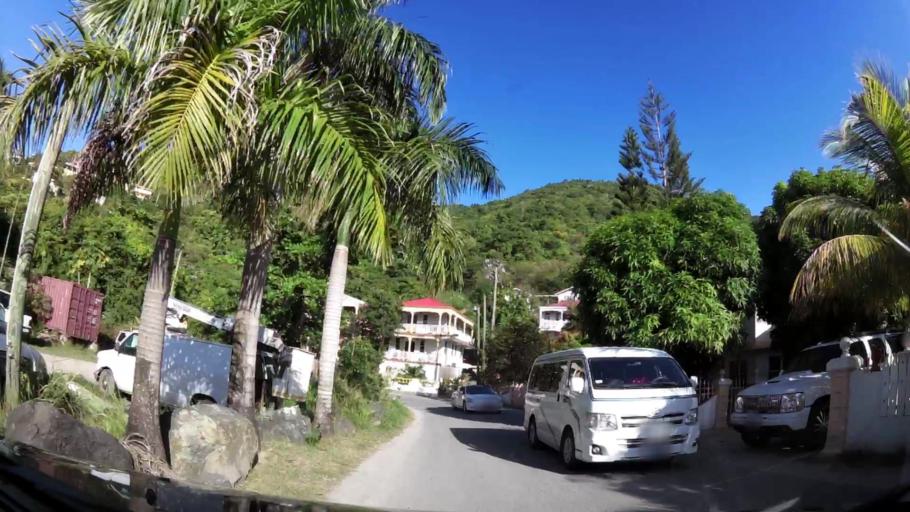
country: VG
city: Road Town
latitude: 18.4258
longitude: -64.6564
